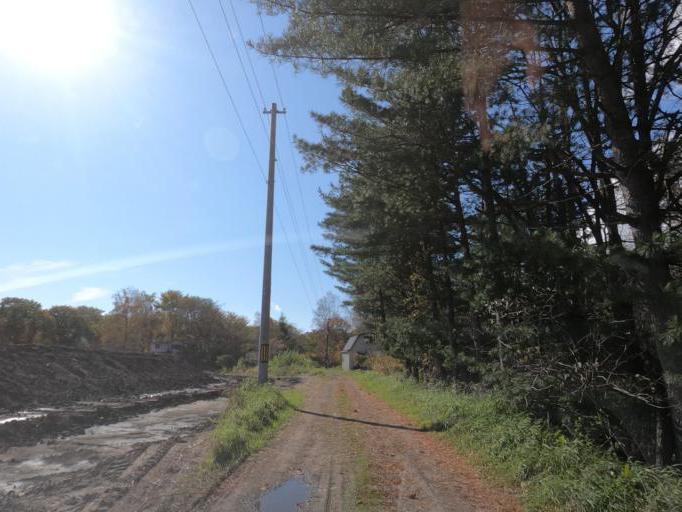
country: JP
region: Hokkaido
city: Otofuke
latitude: 43.2343
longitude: 143.2641
